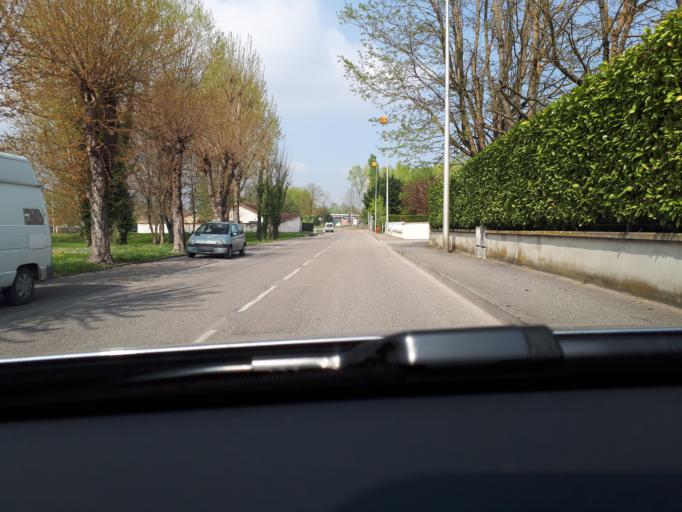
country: FR
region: Rhone-Alpes
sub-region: Departement de l'Isere
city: Bourgoin-Jallieu
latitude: 45.6121
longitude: 5.2704
